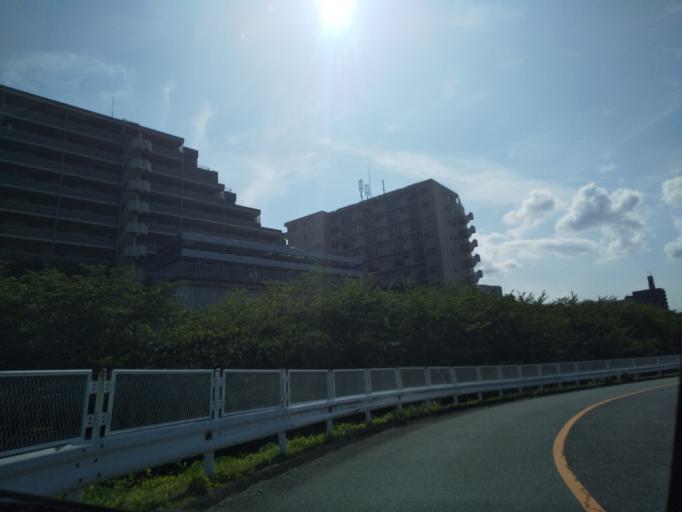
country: JP
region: Kanagawa
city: Zama
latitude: 35.4684
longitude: 139.4145
